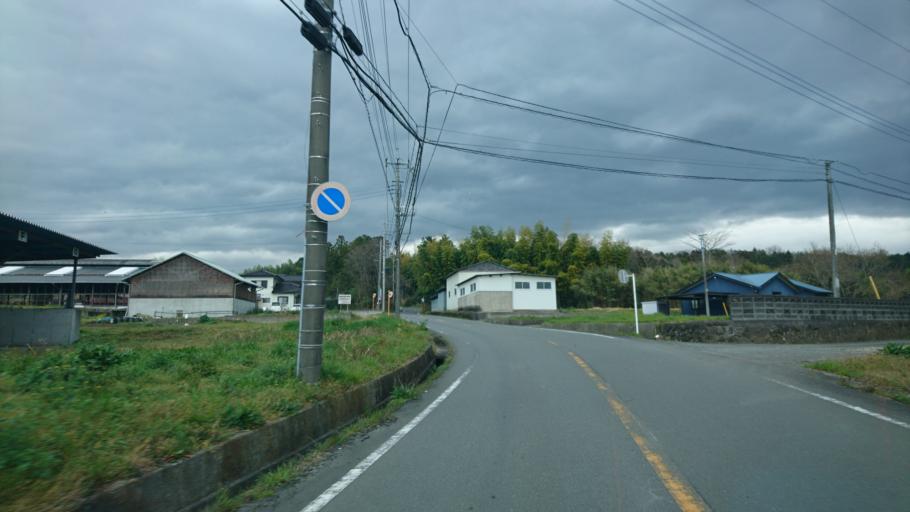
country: JP
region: Shizuoka
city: Fujinomiya
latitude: 35.2631
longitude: 138.6015
